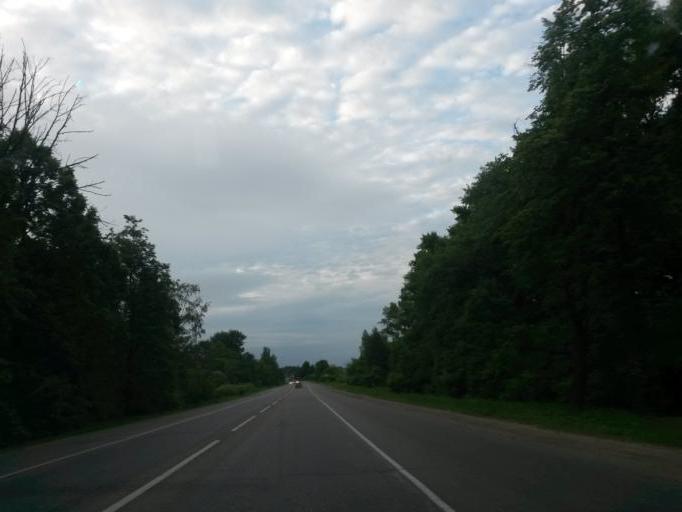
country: RU
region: Moskovskaya
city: Stolbovaya
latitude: 55.2392
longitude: 37.5044
